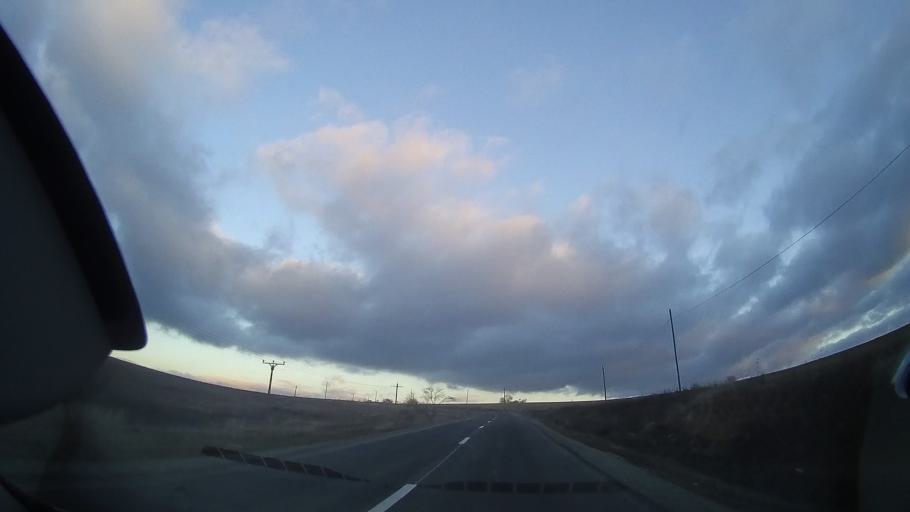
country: RO
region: Cluj
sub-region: Comuna Izvoru Crisului
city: Izvoru Crisului
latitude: 46.8142
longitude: 23.1284
